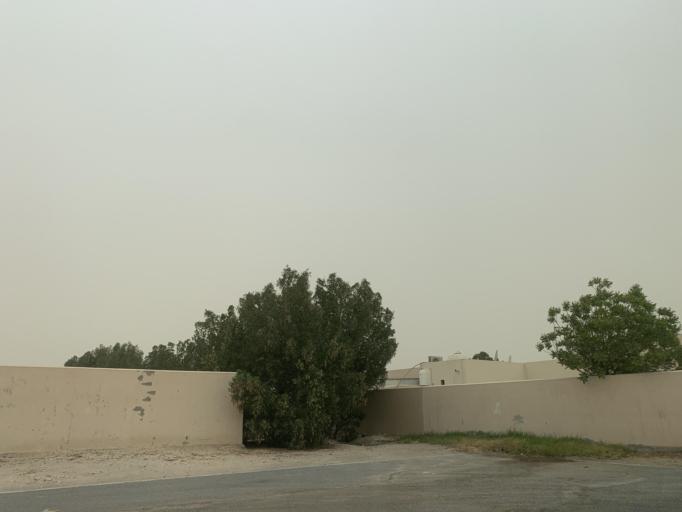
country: BH
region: Central Governorate
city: Madinat Hamad
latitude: 26.1328
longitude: 50.5259
